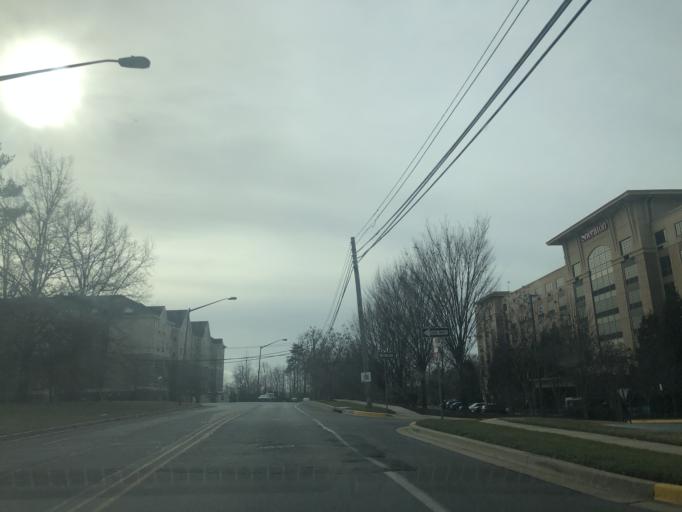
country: US
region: Maryland
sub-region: Howard County
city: Elkridge
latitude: 39.2062
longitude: -76.6923
